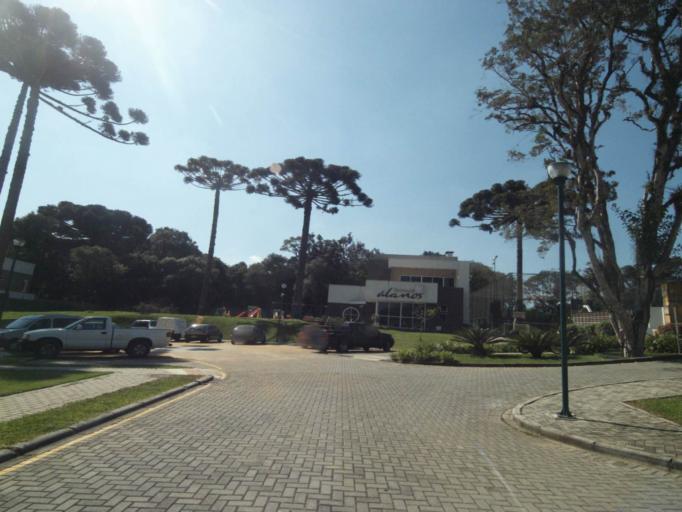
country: BR
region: Parana
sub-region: Curitiba
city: Curitiba
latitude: -25.3836
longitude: -49.2821
